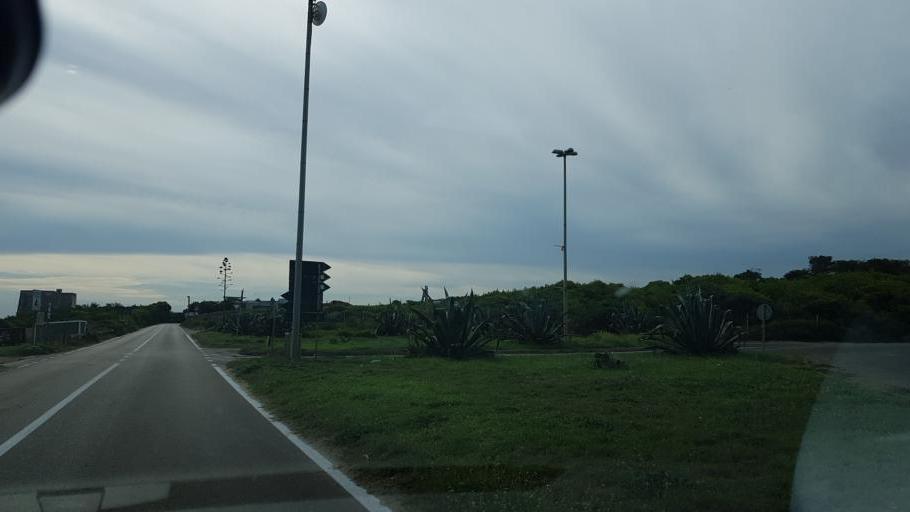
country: IT
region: Apulia
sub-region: Provincia di Lecce
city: Melendugno
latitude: 40.3297
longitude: 18.3729
